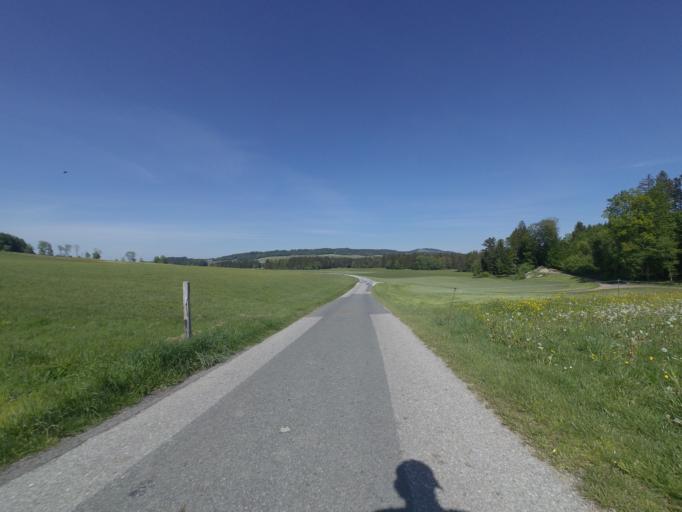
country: AT
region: Salzburg
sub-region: Politischer Bezirk Salzburg-Umgebung
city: Mattsee
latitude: 47.9478
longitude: 13.1184
